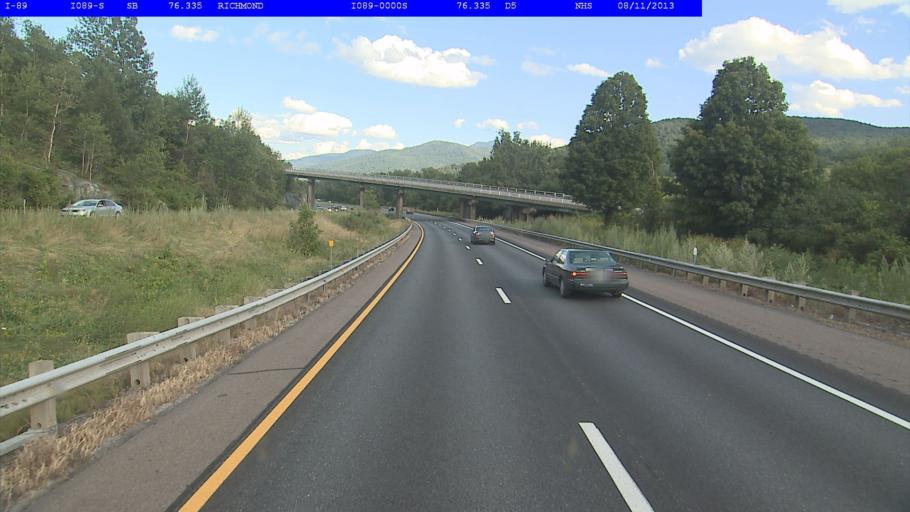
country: US
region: Vermont
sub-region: Chittenden County
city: Williston
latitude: 44.4017
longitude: -72.9861
